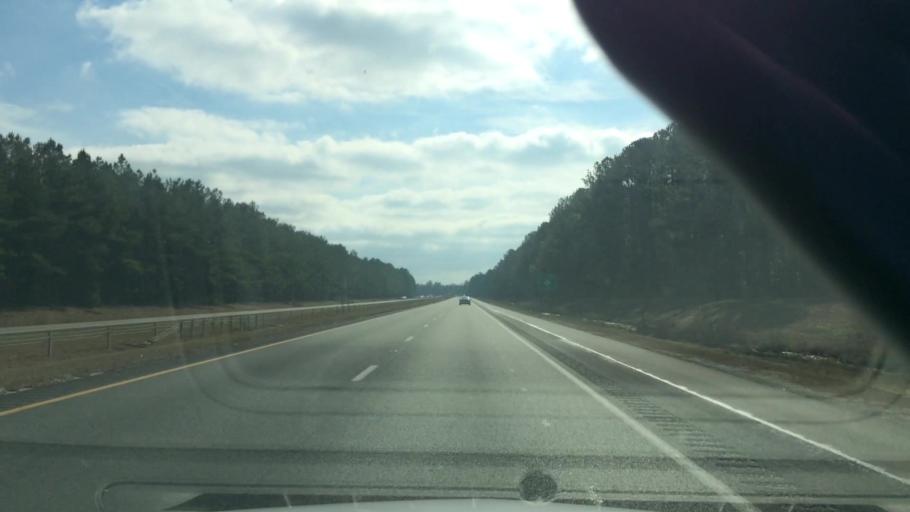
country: US
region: North Carolina
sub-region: Pender County
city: Rocky Point
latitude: 34.4739
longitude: -77.8795
